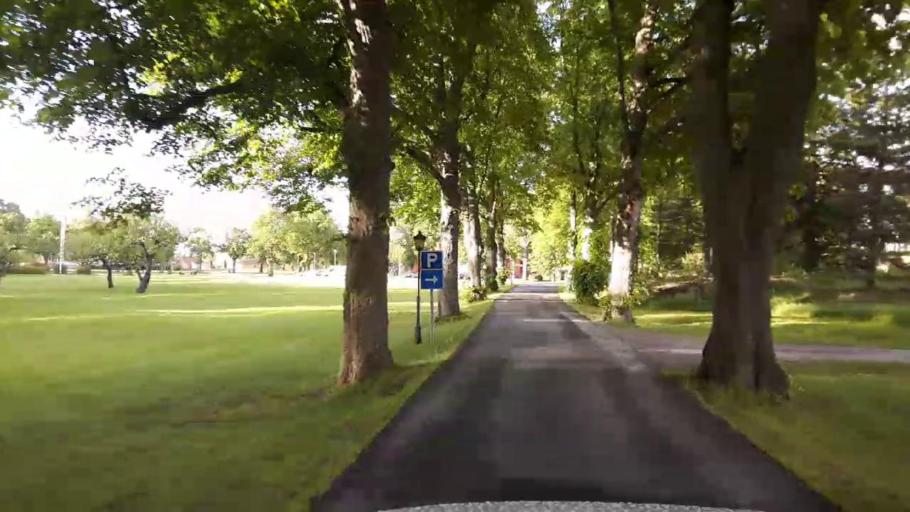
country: SE
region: Stockholm
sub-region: Upplands-Bro Kommun
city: Bro
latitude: 59.5230
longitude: 17.6721
